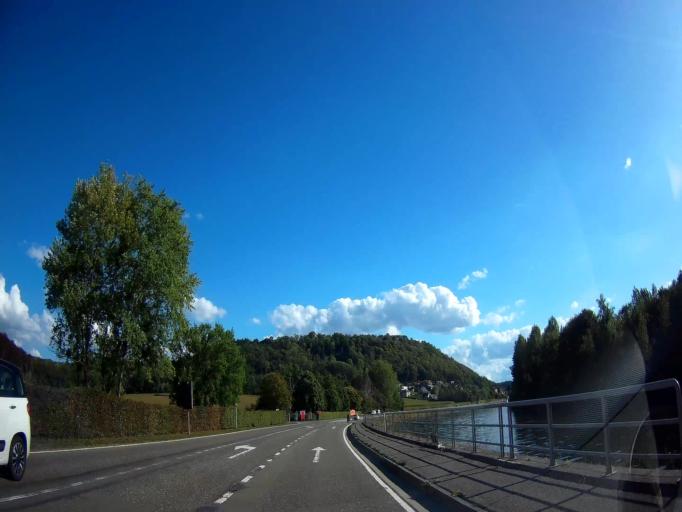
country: BE
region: Wallonia
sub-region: Province de Namur
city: Anhee
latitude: 50.3005
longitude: 4.8989
